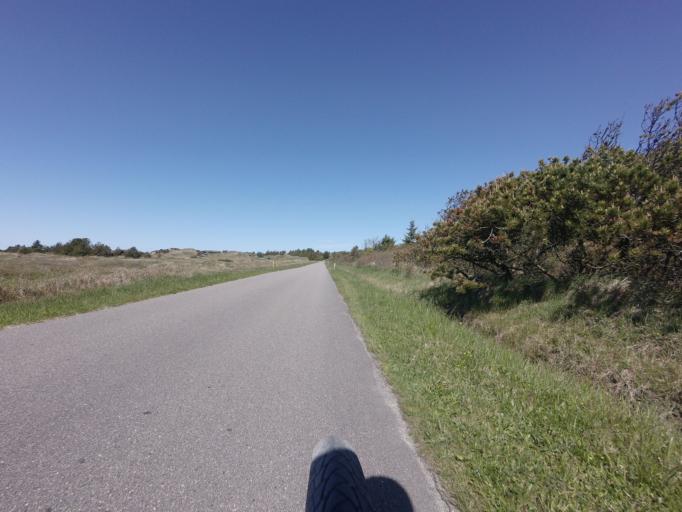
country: DK
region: North Denmark
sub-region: Jammerbugt Kommune
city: Kas
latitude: 57.2269
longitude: 9.5671
